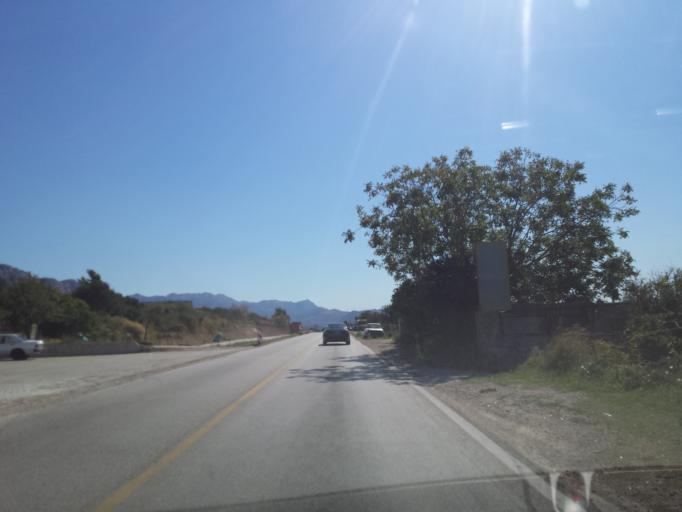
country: HR
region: Splitsko-Dalmatinska
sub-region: Grad Split
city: Split
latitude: 43.5559
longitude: 16.3946
